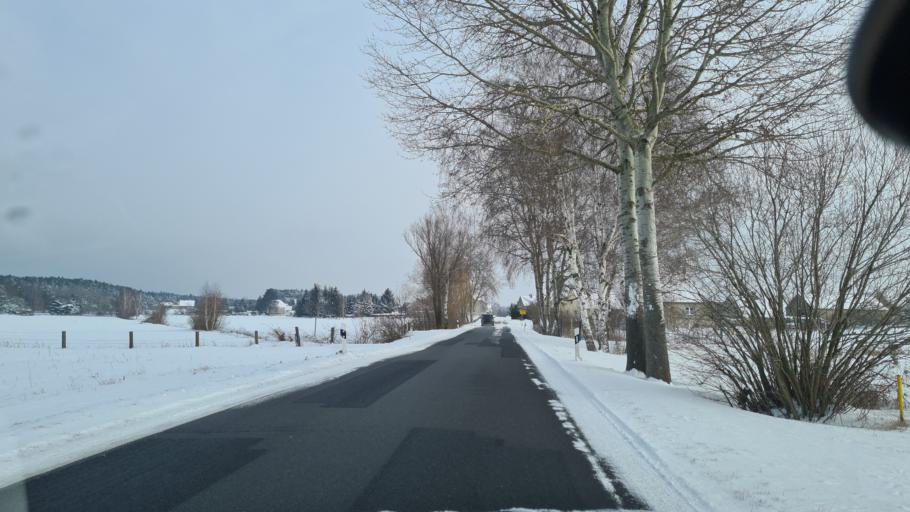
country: DE
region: Brandenburg
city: Schilda
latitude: 51.6114
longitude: 13.3773
